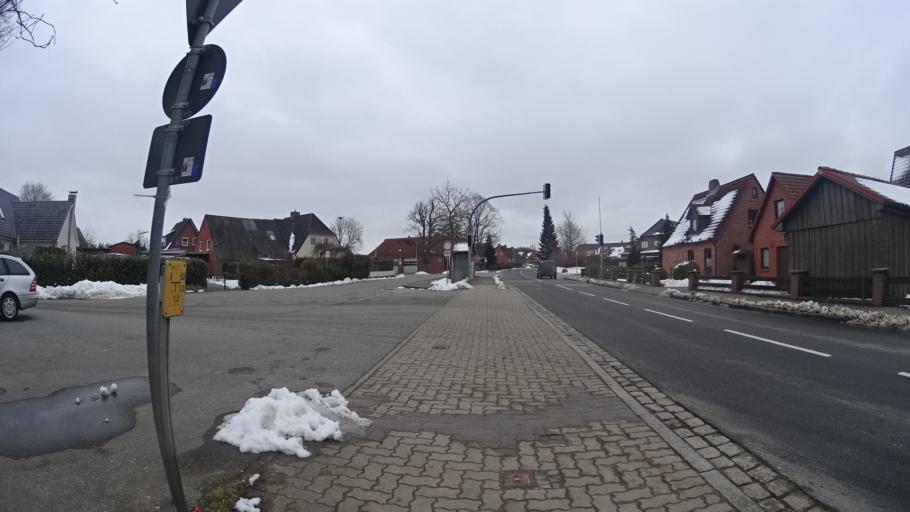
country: DE
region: Schleswig-Holstein
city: Panker
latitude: 54.3133
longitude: 10.5700
